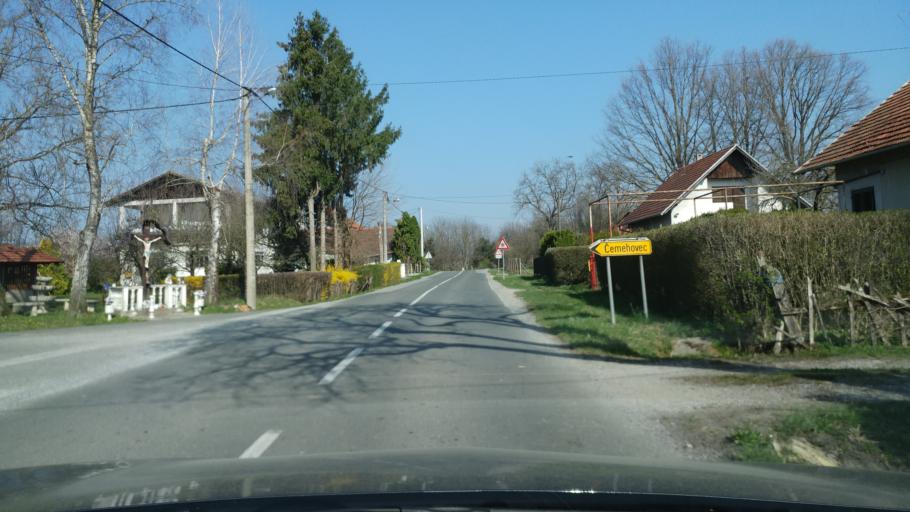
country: HR
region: Zagrebacka
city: Pojatno
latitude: 45.9790
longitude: 15.7316
